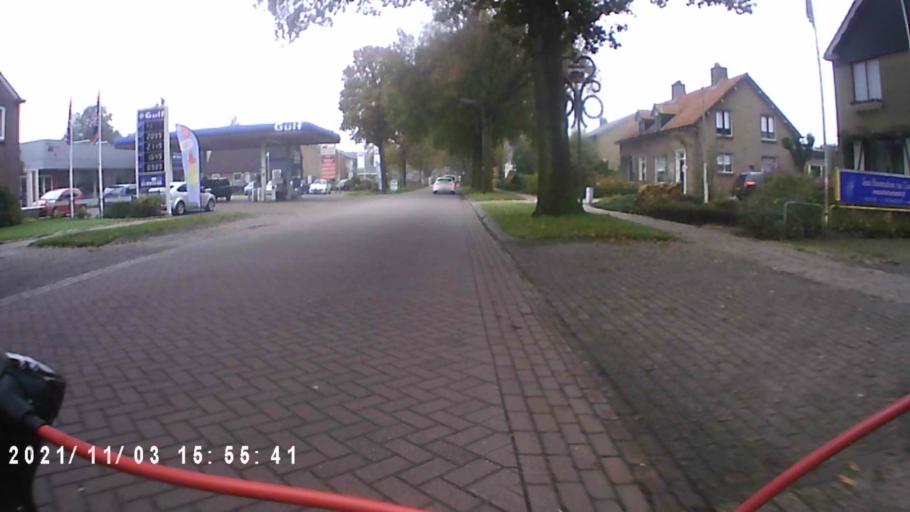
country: NL
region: Groningen
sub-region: Gemeente Leek
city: Leek
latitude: 53.0645
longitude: 6.3312
